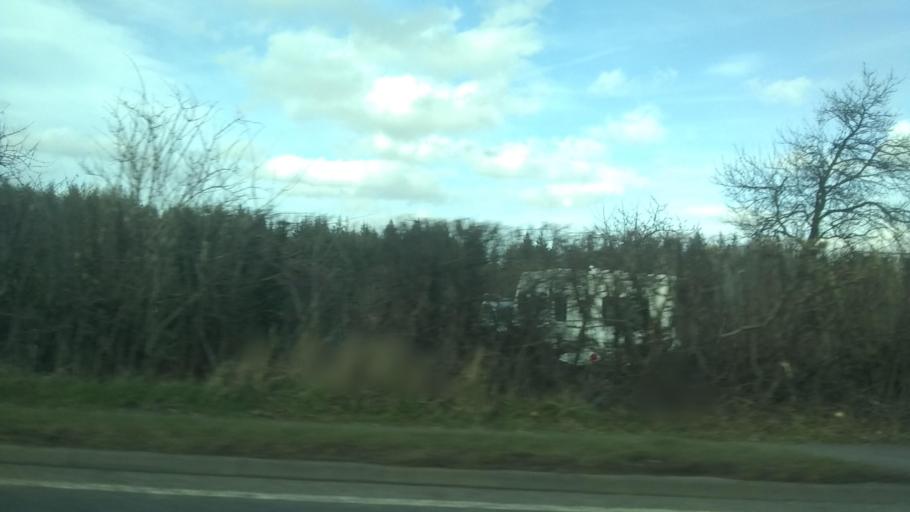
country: GB
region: England
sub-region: Worcestershire
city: Bewdley
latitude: 52.3620
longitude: -2.3727
